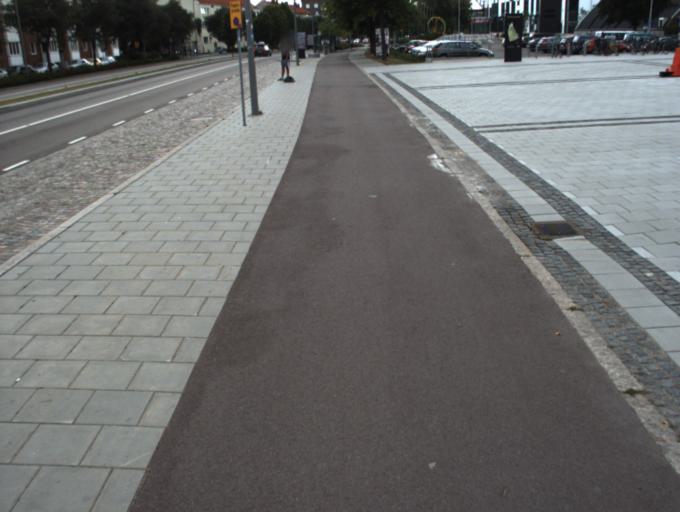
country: SE
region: Skane
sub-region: Helsingborg
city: Helsingborg
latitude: 56.0512
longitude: 12.7051
